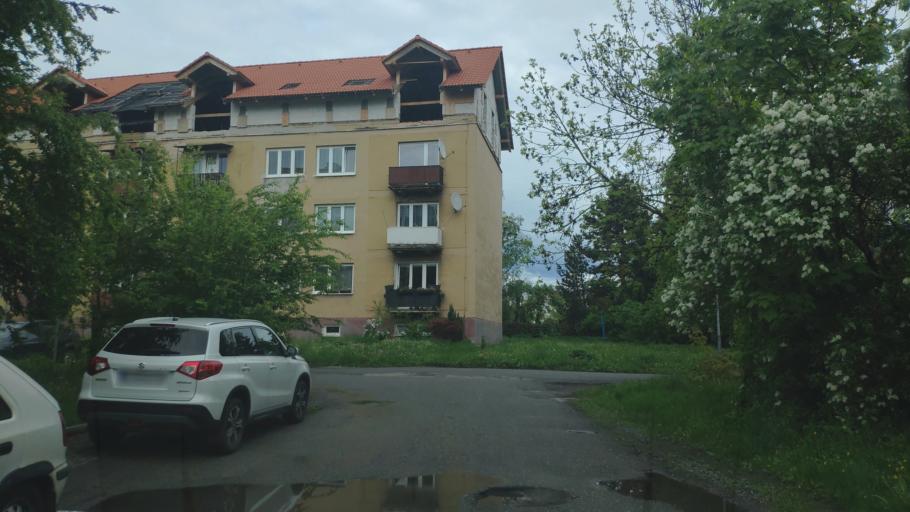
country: SK
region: Presovsky
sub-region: Okres Presov
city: Presov
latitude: 48.9986
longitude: 21.2343
